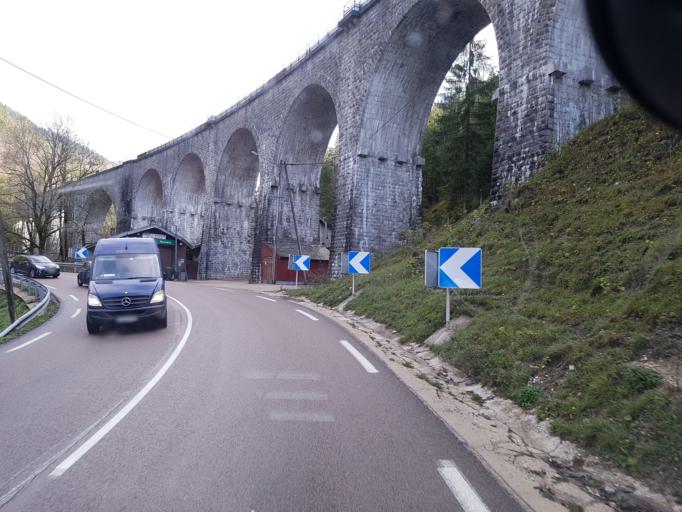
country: FR
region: Franche-Comte
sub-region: Departement du Jura
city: Morez
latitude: 46.5352
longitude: 6.0275
